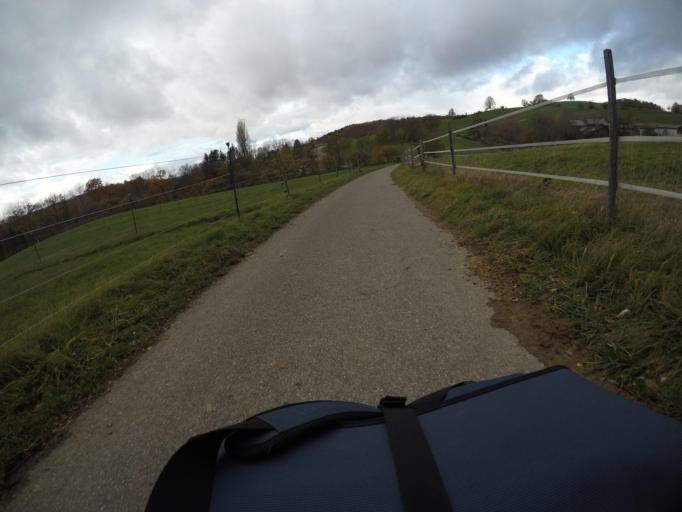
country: DE
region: Baden-Wuerttemberg
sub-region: Tuebingen Region
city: Gomaringen
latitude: 48.4479
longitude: 9.1473
